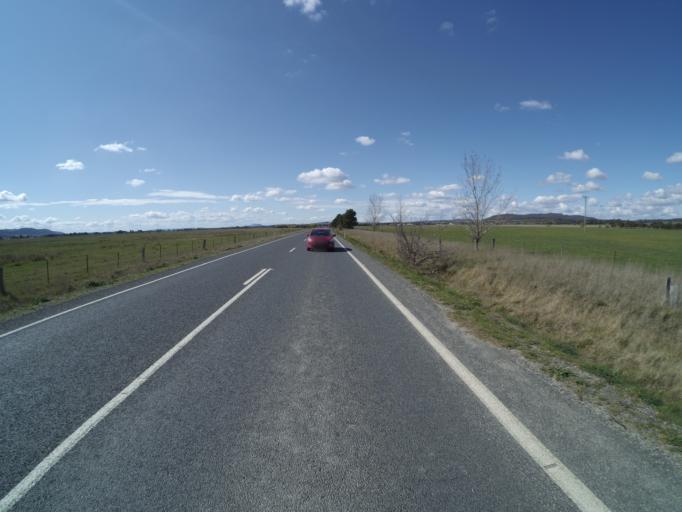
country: AU
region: New South Wales
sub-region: Palerang
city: Bungendore
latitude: -35.2766
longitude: 149.4245
